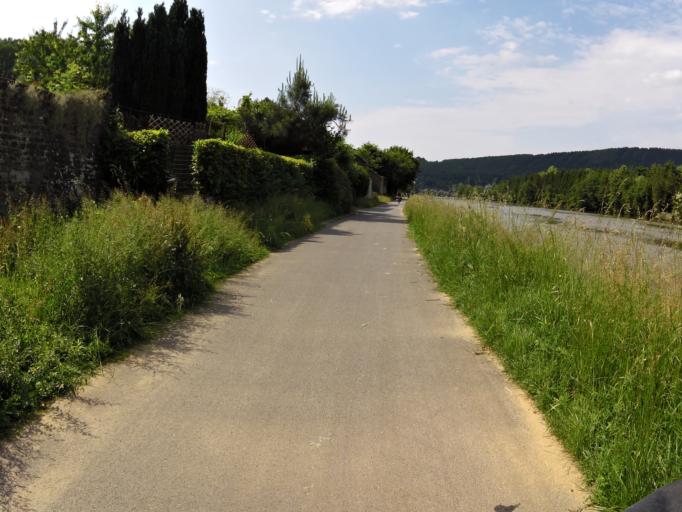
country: FR
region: Champagne-Ardenne
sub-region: Departement des Ardennes
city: Nouzonville
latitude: 49.8534
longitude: 4.7631
